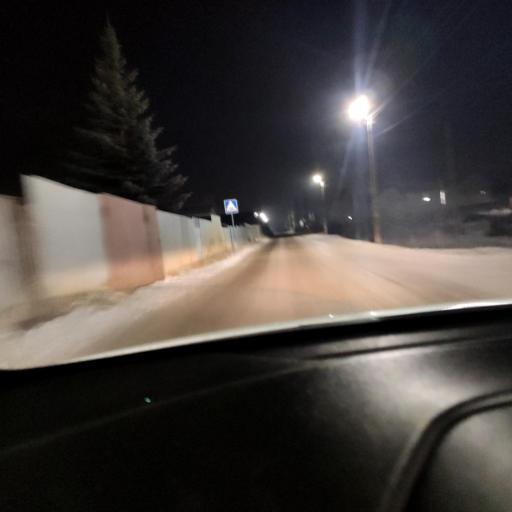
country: RU
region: Tatarstan
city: Staroye Arakchino
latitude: 55.8823
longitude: 49.0404
